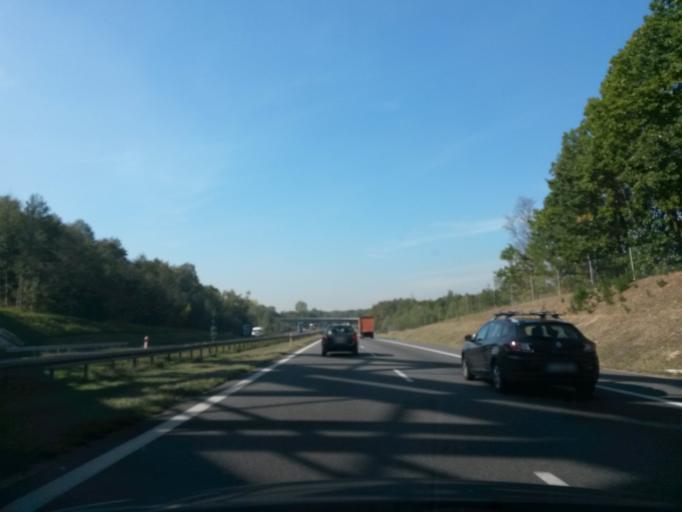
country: PL
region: Silesian Voivodeship
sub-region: Katowice
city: Murcki
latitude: 50.2286
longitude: 19.0744
